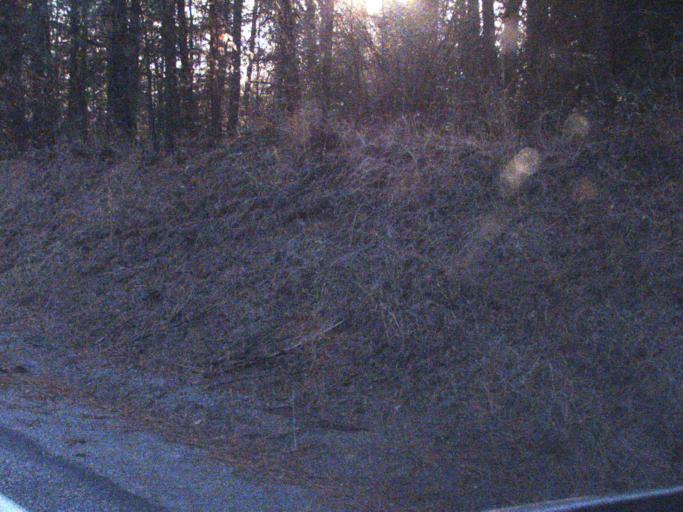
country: US
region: Washington
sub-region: Stevens County
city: Kettle Falls
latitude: 48.7910
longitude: -117.9989
